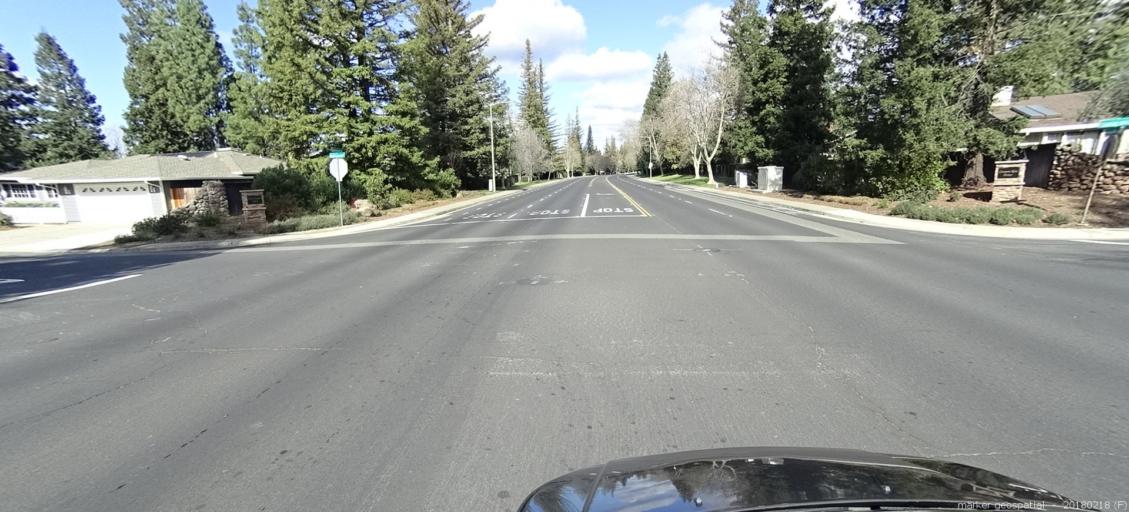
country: US
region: California
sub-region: Sacramento County
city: Folsom
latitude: 38.6887
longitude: -121.1869
